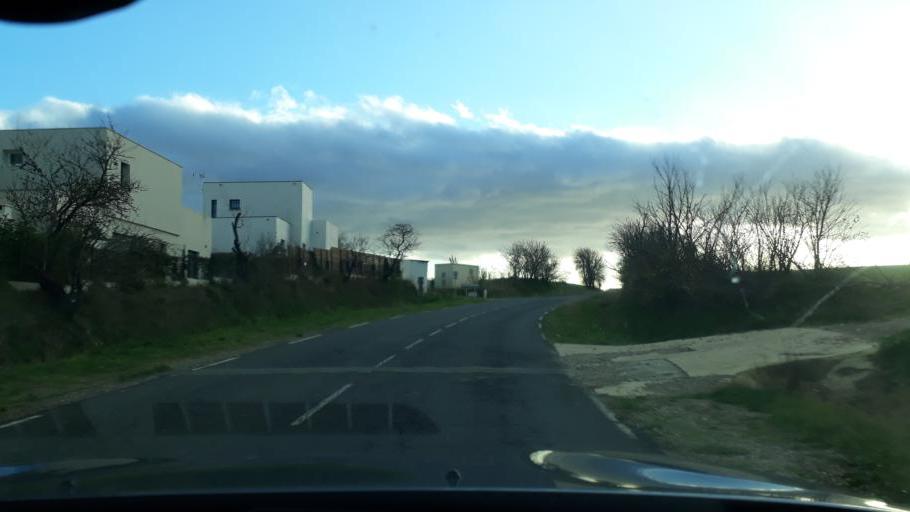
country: FR
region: Languedoc-Roussillon
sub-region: Departement de l'Herault
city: Colombiers
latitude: 43.3084
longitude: 3.1391
